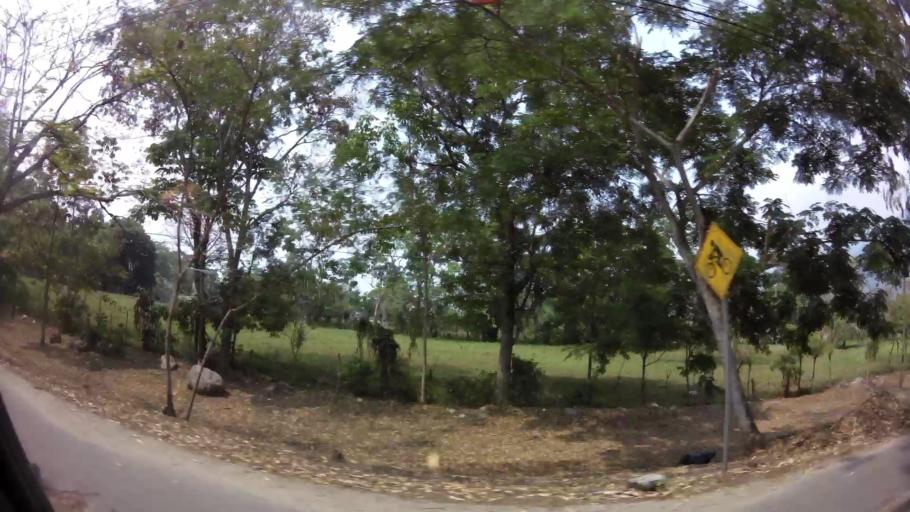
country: HN
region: Cortes
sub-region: San Pedro Sula
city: Pena Blanca
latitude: 15.5654
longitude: -88.0259
